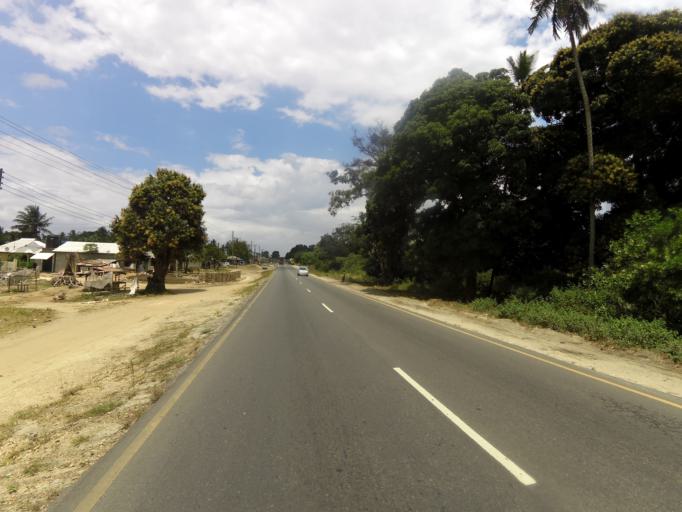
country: TZ
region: Pwani
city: Vikindu
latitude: -6.9810
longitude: 39.2916
